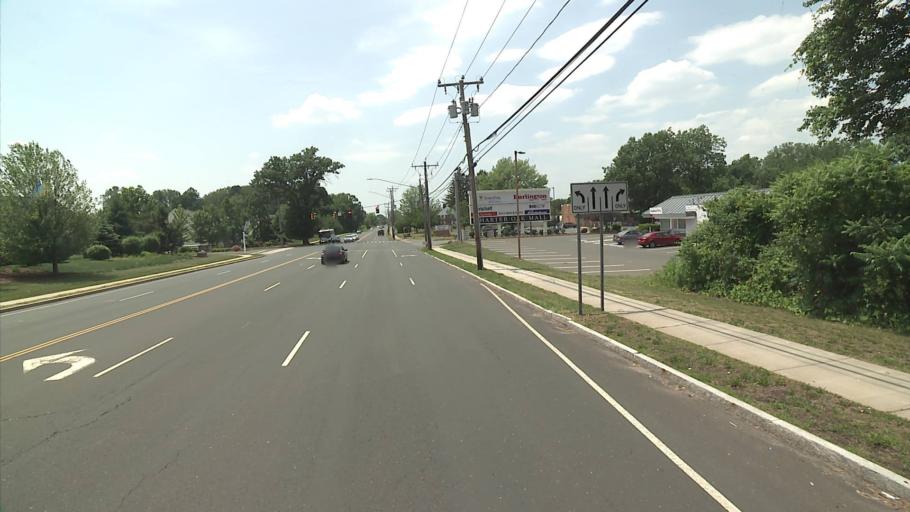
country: US
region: Connecticut
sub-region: Hartford County
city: East Hartford
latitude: 41.7656
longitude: -72.6020
